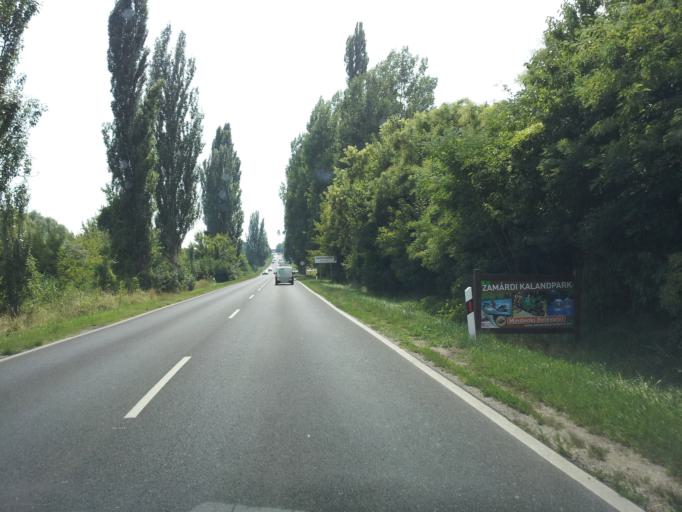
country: HU
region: Veszprem
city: Balatonalmadi
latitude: 47.0673
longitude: 18.0313
